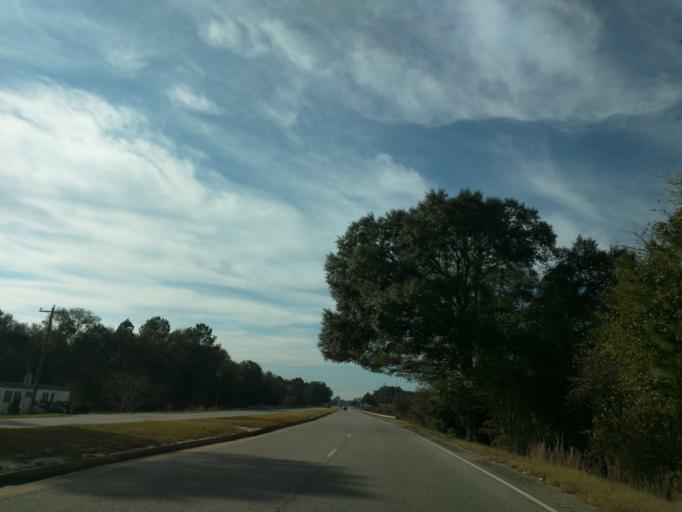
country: US
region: Georgia
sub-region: Decatur County
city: Bainbridge
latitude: 30.9019
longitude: -84.5278
